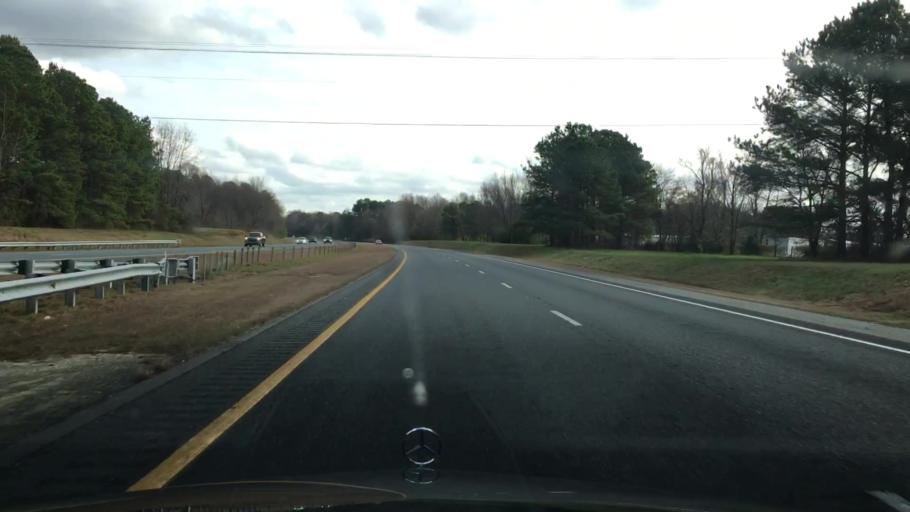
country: US
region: North Carolina
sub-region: Sampson County
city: Clinton
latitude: 35.2141
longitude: -78.3286
